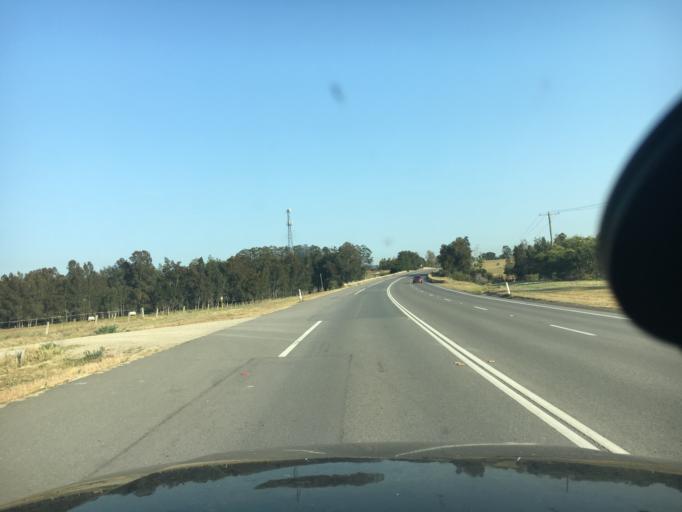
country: AU
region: New South Wales
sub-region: Cessnock
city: Branxton
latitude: -32.6618
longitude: 151.3673
